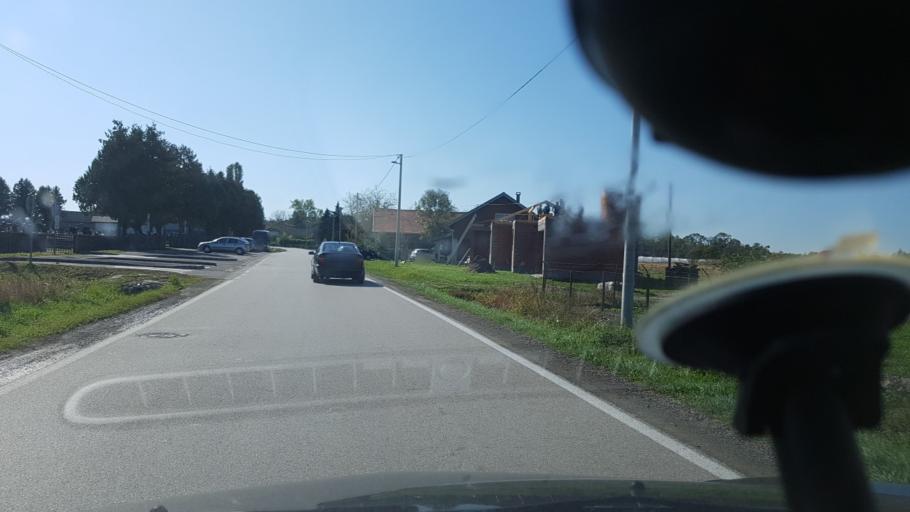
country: HR
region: Zagrebacka
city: Lupoglav
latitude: 45.7403
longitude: 16.3022
